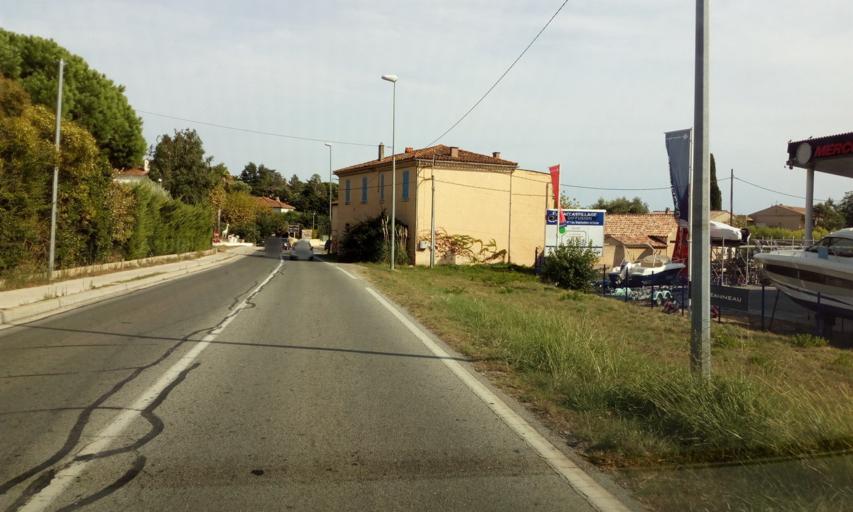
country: FR
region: Provence-Alpes-Cote d'Azur
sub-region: Departement du Var
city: Bormes-les-Mimosas
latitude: 43.1417
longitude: 6.3487
